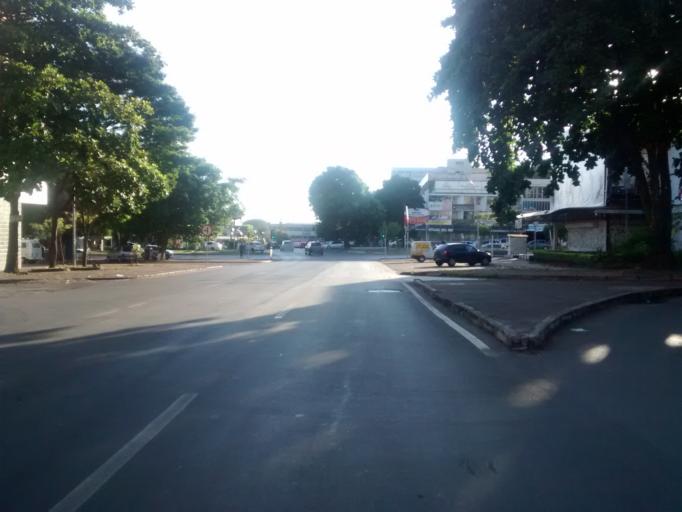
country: BR
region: Federal District
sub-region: Brasilia
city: Brasilia
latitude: -15.7698
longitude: -47.8900
